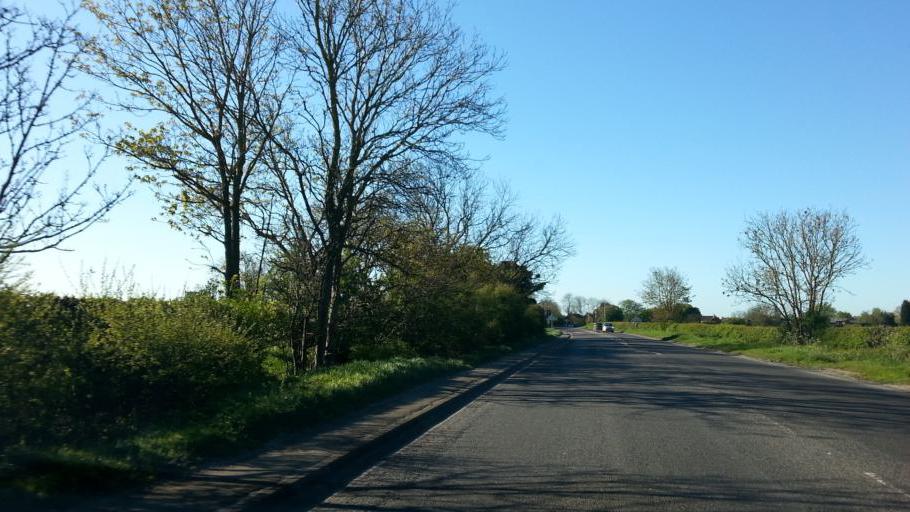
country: GB
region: England
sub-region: Nottinghamshire
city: Newark on Trent
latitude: 53.1113
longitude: -0.8203
